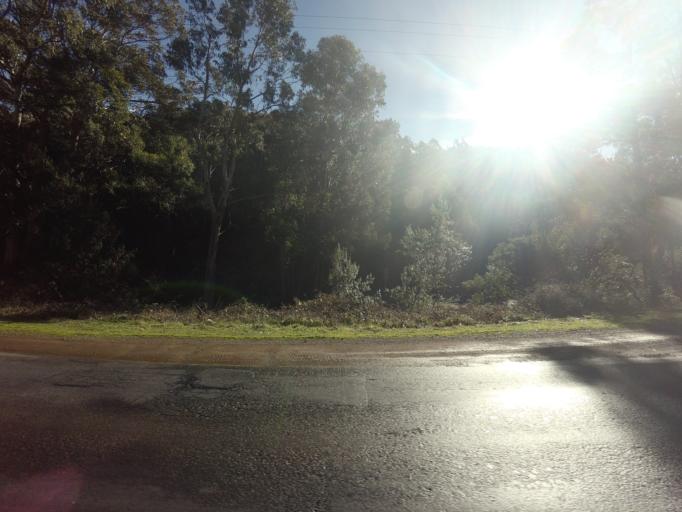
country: AU
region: Tasmania
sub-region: Glenorchy
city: Berriedale
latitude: -42.8184
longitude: 147.2204
